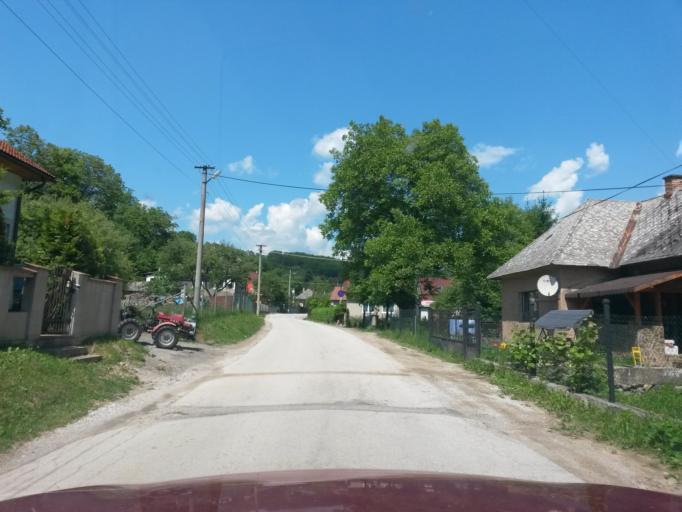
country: SK
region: Kosicky
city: Roznava
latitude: 48.6896
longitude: 20.5430
